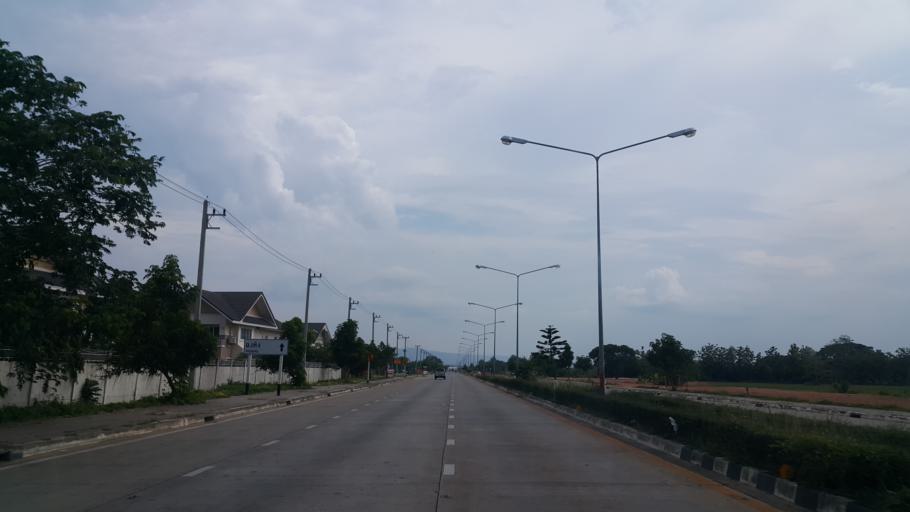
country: TH
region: Chiang Rai
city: Chiang Rai
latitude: 19.9037
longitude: 99.8589
